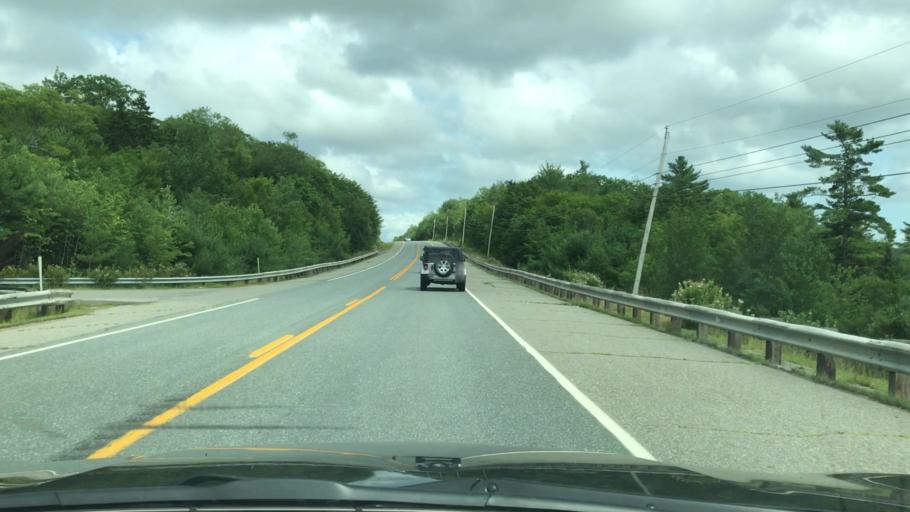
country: US
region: Maine
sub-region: Hancock County
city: Surry
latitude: 44.5650
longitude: -68.6052
